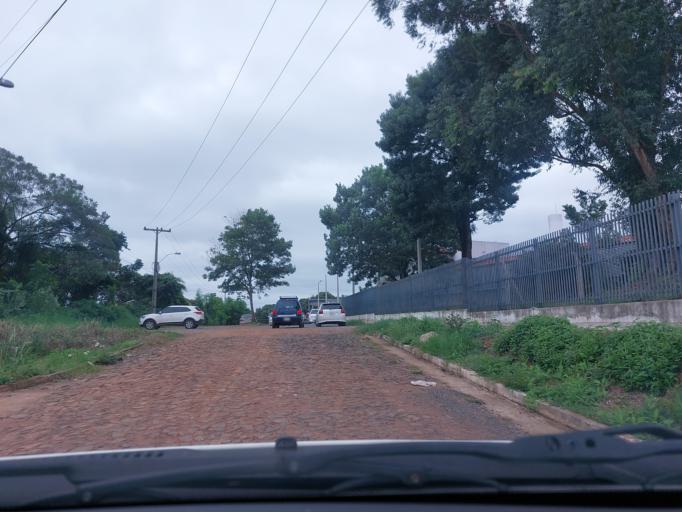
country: PY
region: San Pedro
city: Guayaybi
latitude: -24.6653
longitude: -56.4314
